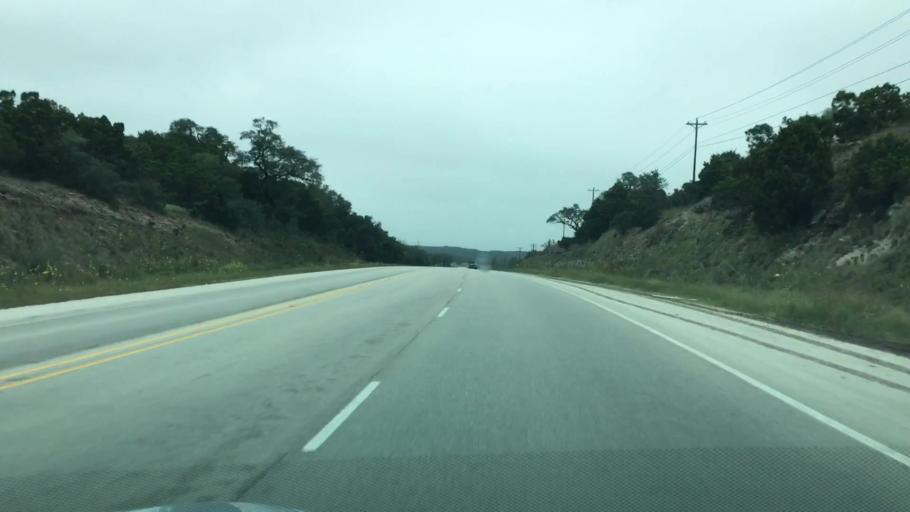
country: US
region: Texas
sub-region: Blanco County
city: Blanco
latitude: 29.9636
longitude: -98.4098
